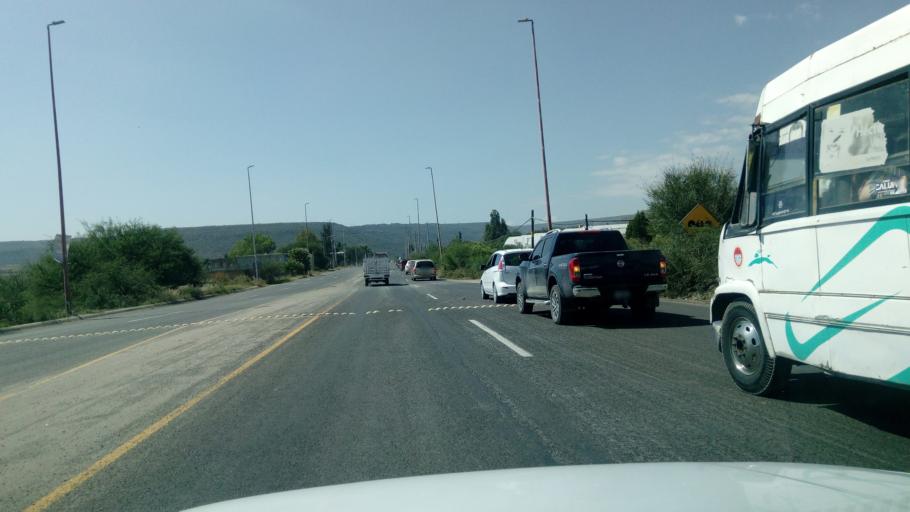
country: MX
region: Durango
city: Victoria de Durango
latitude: 23.9727
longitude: -104.6981
